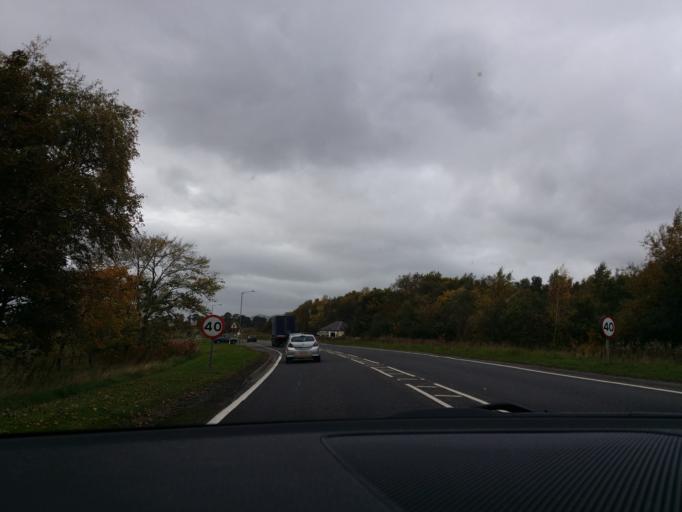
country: GB
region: Scotland
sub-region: Clackmannanshire
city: Clackmannan
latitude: 56.1128
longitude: -3.7471
